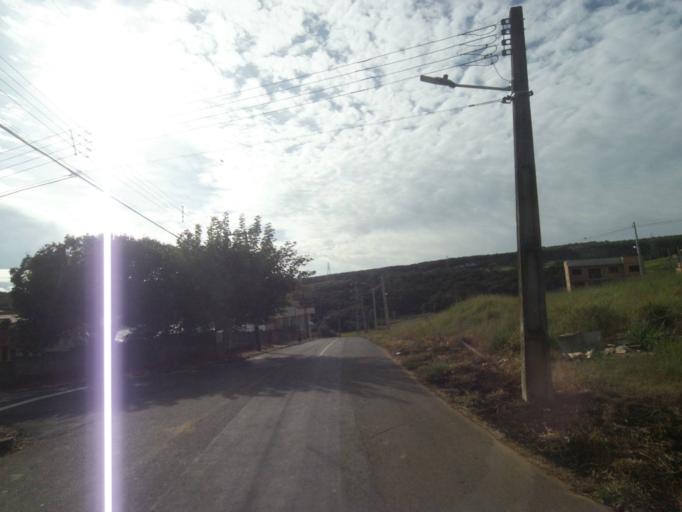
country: BR
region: Parana
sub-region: Telemaco Borba
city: Telemaco Borba
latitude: -24.3450
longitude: -50.6067
